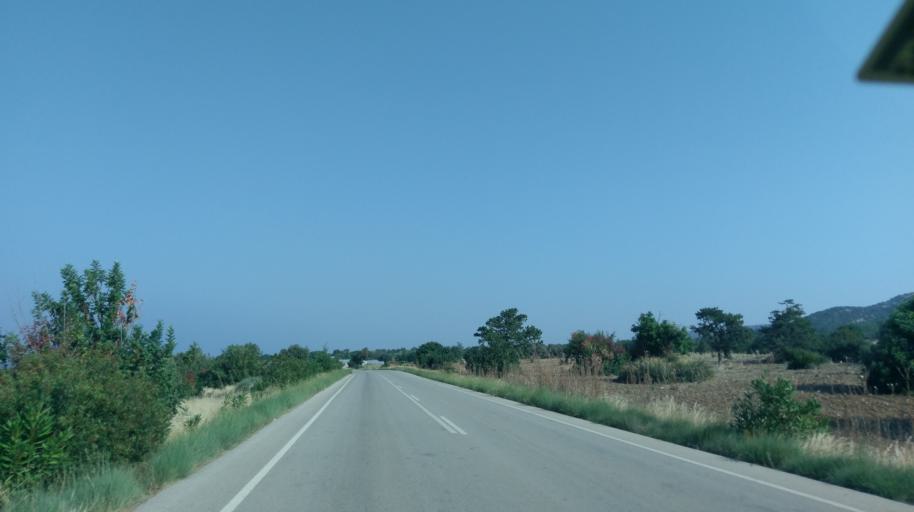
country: CY
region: Ammochostos
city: Lefkonoiko
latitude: 35.3778
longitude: 33.7180
